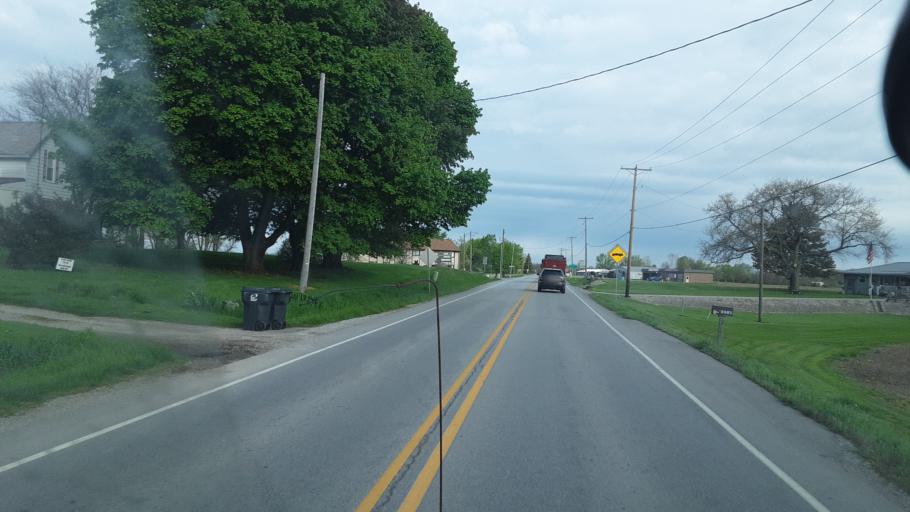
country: US
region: Indiana
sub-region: Whitley County
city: Churubusco
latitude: 41.2380
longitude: -85.3248
